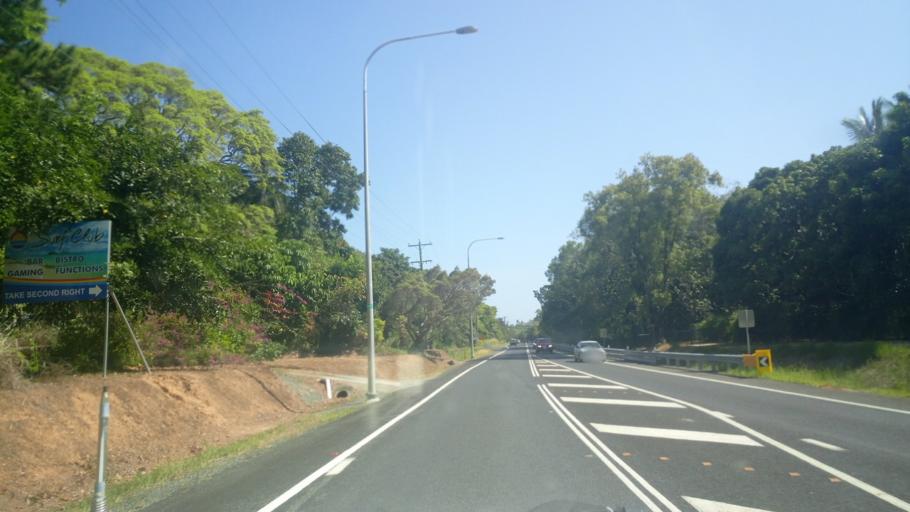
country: AU
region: Queensland
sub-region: Cairns
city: Palm Cove
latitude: -16.7511
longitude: 145.6621
